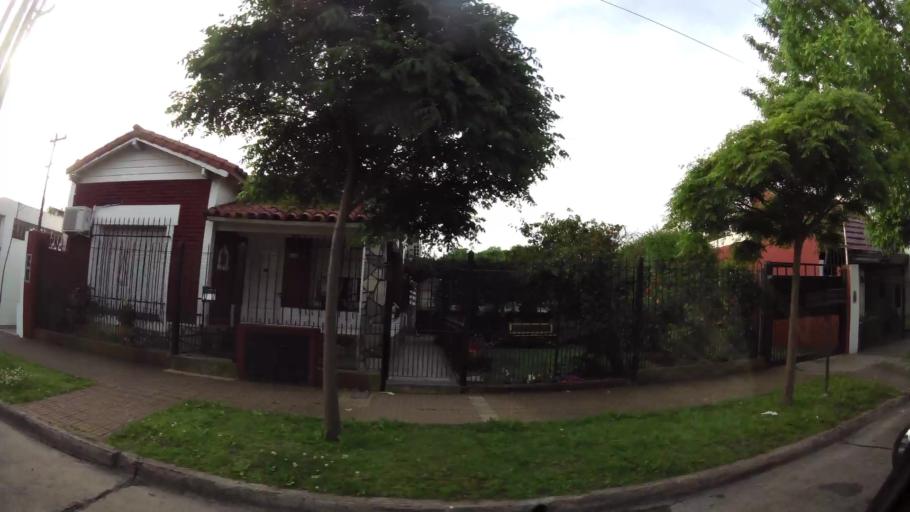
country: AR
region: Buenos Aires
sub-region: Partido de Quilmes
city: Quilmes
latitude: -34.7372
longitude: -58.2679
